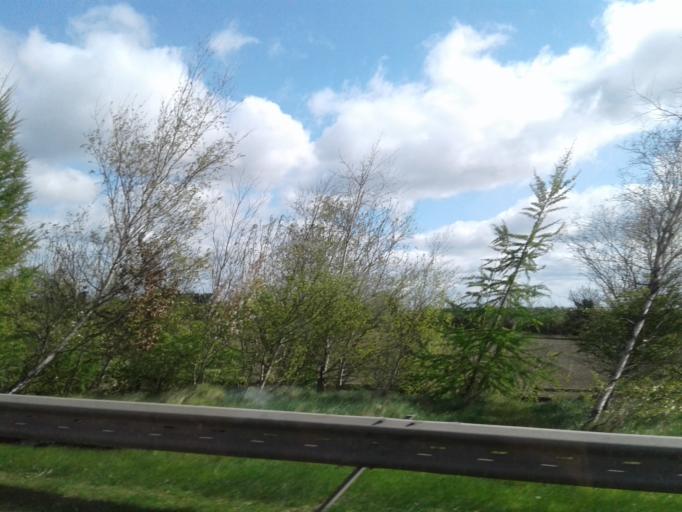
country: IE
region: Leinster
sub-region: Fingal County
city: Blanchardstown
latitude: 53.4512
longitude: -6.3547
